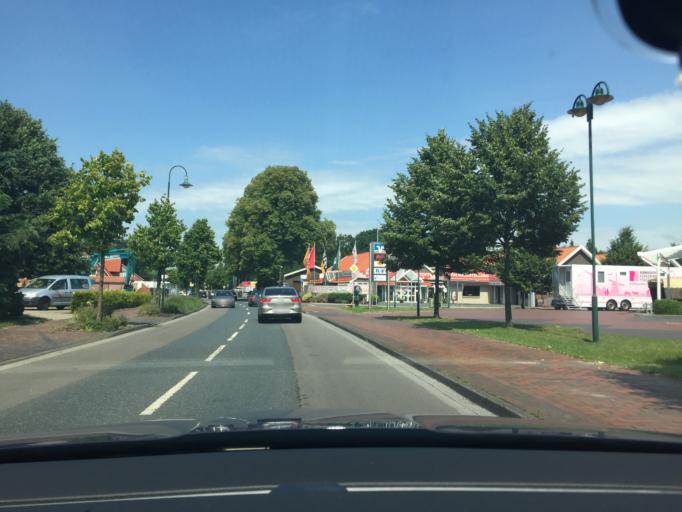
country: DE
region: Lower Saxony
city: Hesel
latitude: 53.3028
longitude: 7.5946
